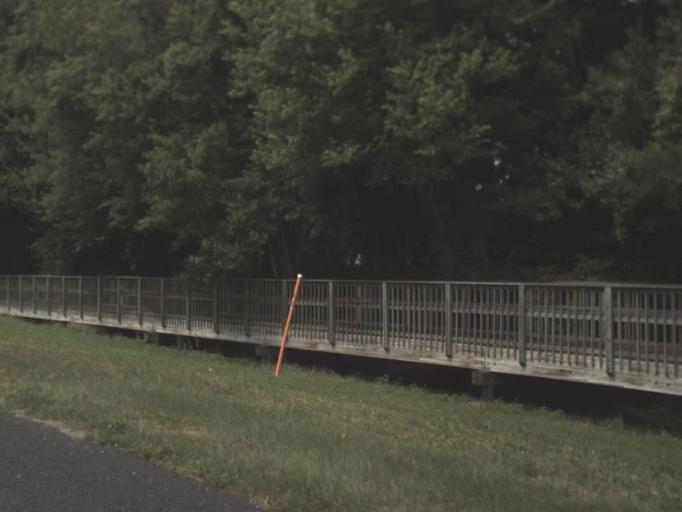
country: US
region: Florida
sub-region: Clay County
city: Orange Park
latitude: 30.1242
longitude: -81.7044
